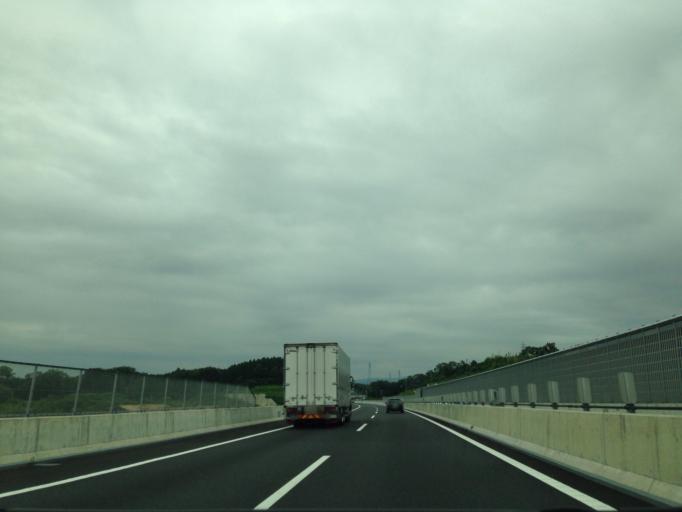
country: JP
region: Aichi
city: Okazaki
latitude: 35.0249
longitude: 137.2249
